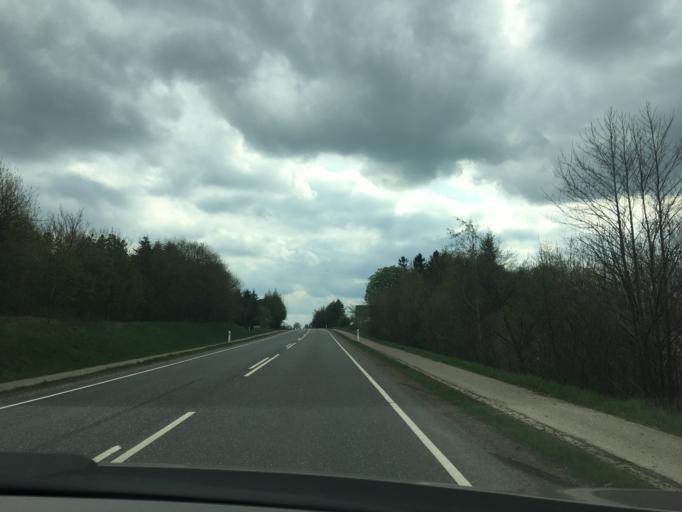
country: DK
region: Central Jutland
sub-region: Horsens Kommune
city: Braedstrup
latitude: 56.0085
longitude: 9.6052
